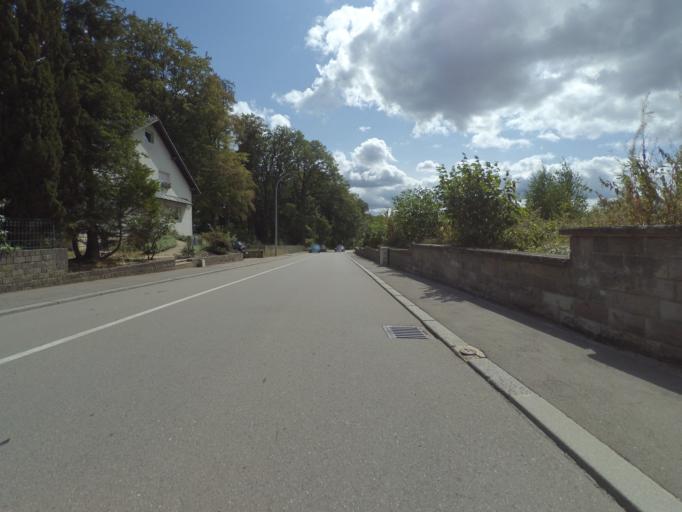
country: LU
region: Luxembourg
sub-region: Canton de Luxembourg
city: Niederanven
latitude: 49.6481
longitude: 6.2273
